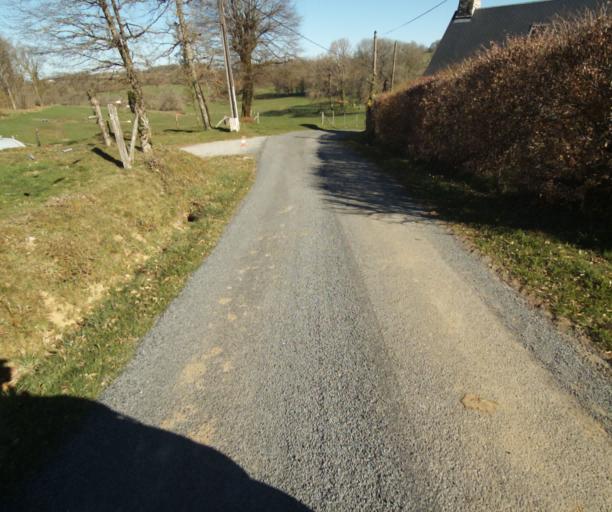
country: FR
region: Limousin
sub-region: Departement de la Correze
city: Seilhac
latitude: 45.3970
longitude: 1.6995
